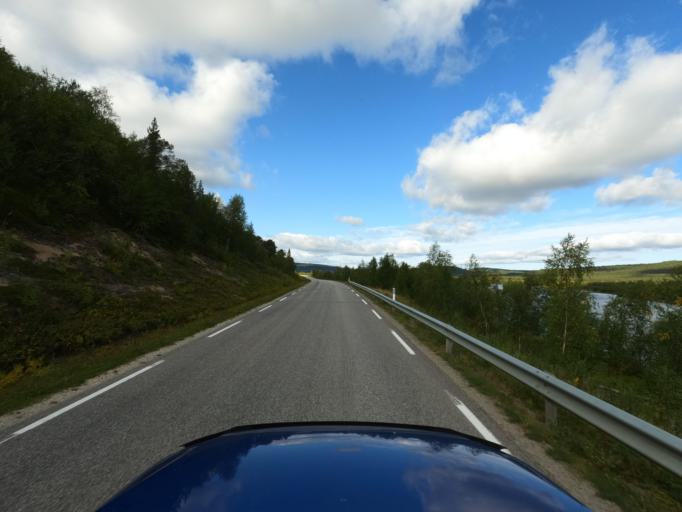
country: NO
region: Finnmark Fylke
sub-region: Karasjok
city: Karasjohka
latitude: 69.4509
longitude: 25.5830
